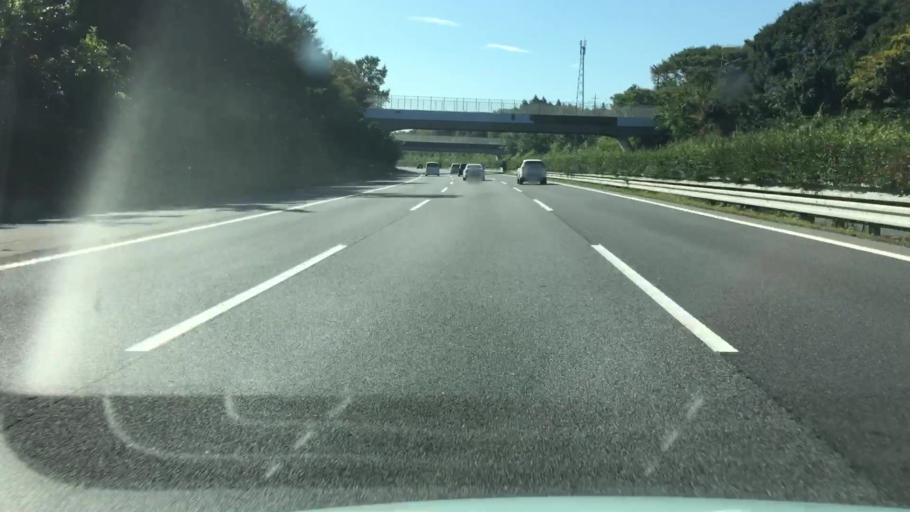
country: JP
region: Ibaraki
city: Naka
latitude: 36.0829
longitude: 140.1551
